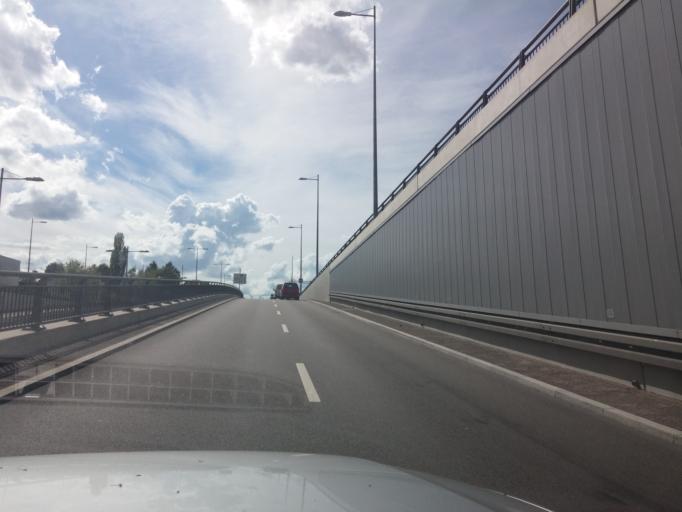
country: DE
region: Bavaria
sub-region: Upper Bavaria
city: Pullach im Isartal
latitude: 48.1101
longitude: 11.5220
